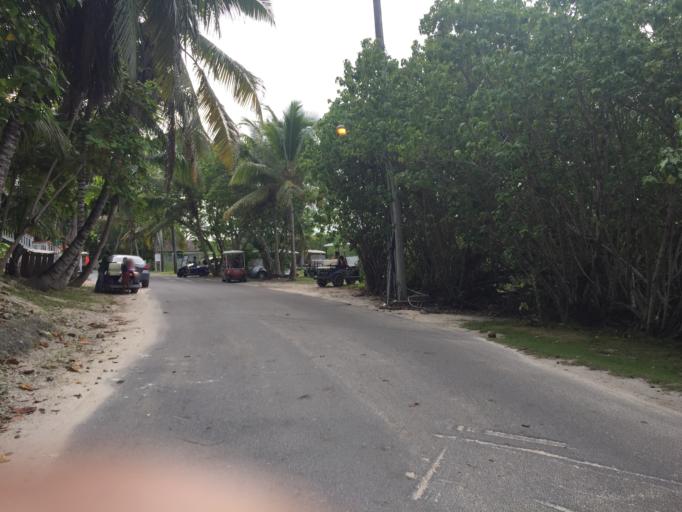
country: BS
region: Central Abaco
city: Marsh Harbour
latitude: 26.5356
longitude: -76.9588
